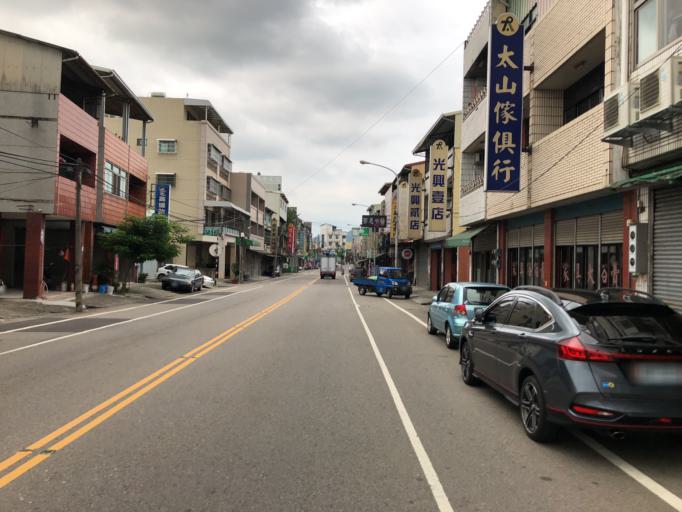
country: TW
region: Taiwan
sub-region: Taichung City
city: Taichung
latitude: 24.1103
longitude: 120.7302
